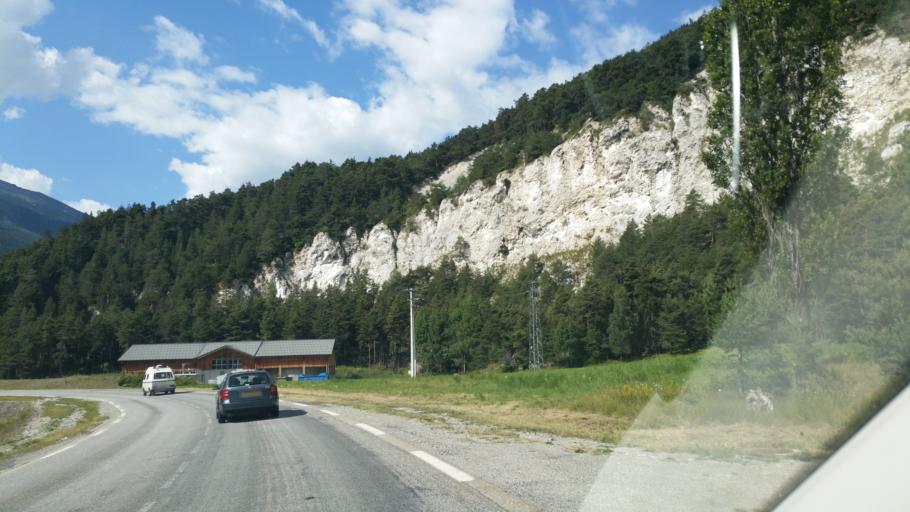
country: FR
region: Rhone-Alpes
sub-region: Departement de la Savoie
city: Modane
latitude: 45.2440
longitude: 6.7929
